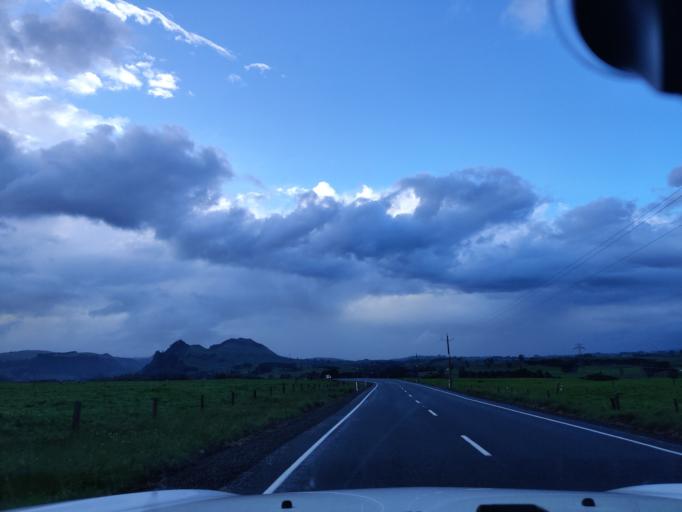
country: NZ
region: Waikato
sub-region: South Waikato District
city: Tokoroa
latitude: -38.4009
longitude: 175.7894
